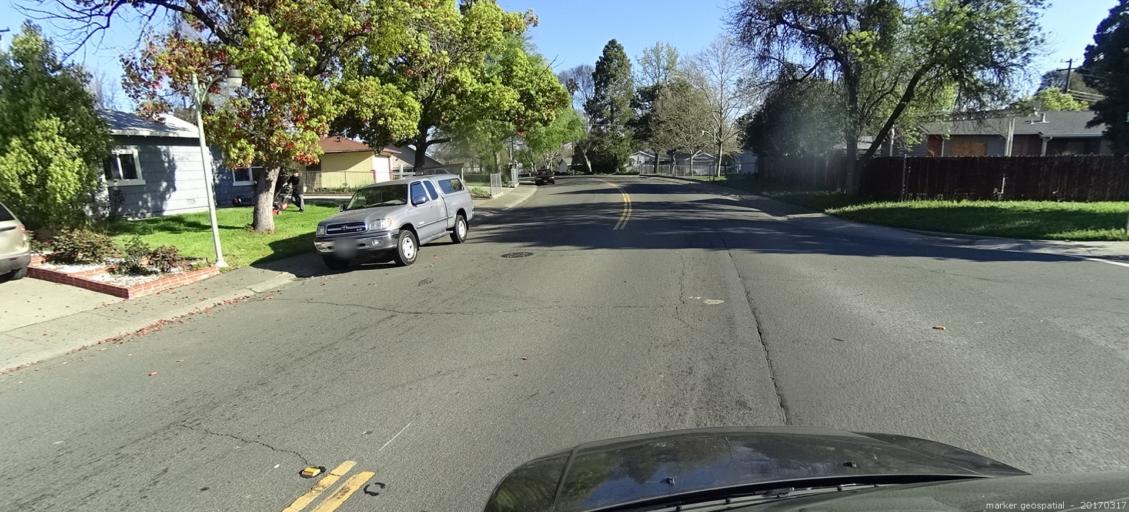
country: US
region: California
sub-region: Sacramento County
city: Parkway
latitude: 38.4942
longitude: -121.5035
